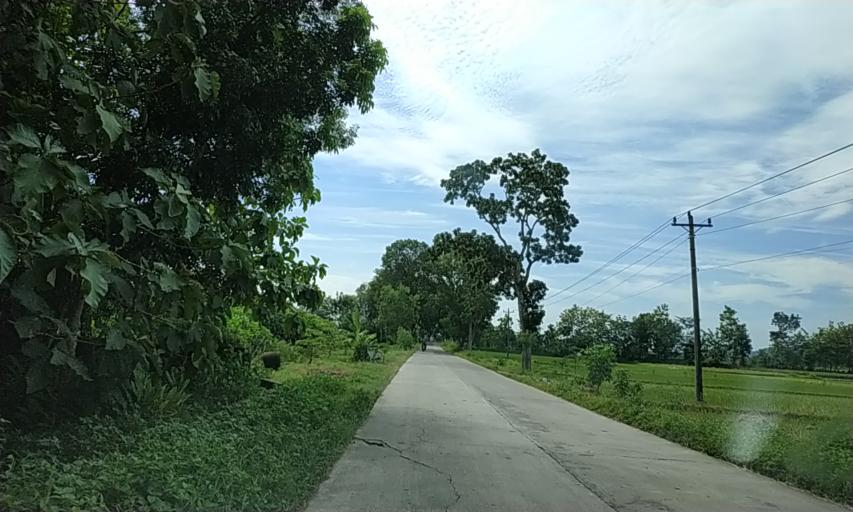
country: ID
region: Central Java
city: Selogiri
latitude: -7.7861
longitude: 110.8779
